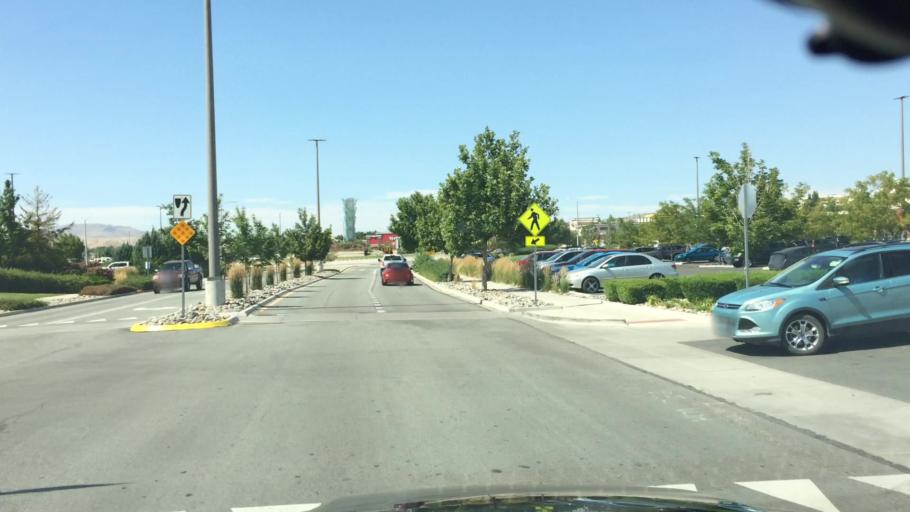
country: US
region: Nevada
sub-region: Washoe County
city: Sparks
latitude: 39.5322
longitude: -119.7188
